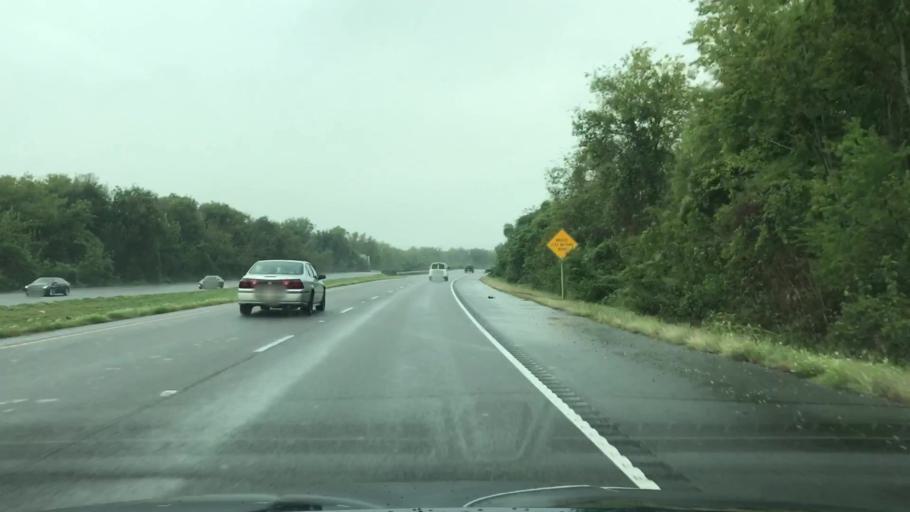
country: US
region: Louisiana
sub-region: Lafourche Parish
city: Raceland
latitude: 29.6936
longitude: -90.5861
